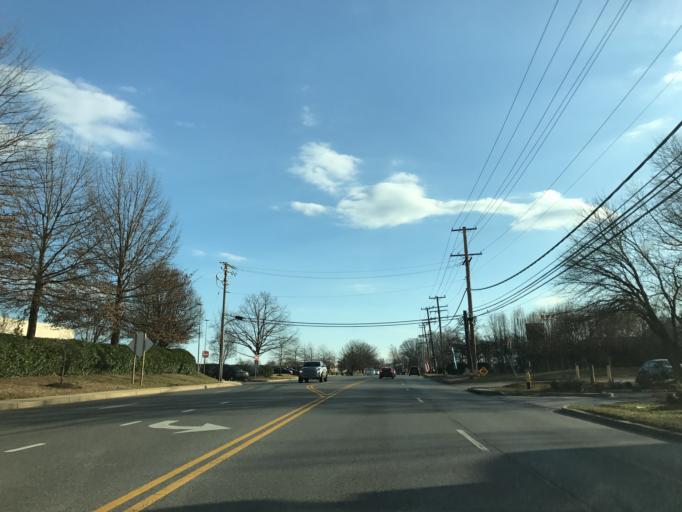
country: US
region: Maryland
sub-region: Anne Arundel County
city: Parole
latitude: 38.9892
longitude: -76.5489
